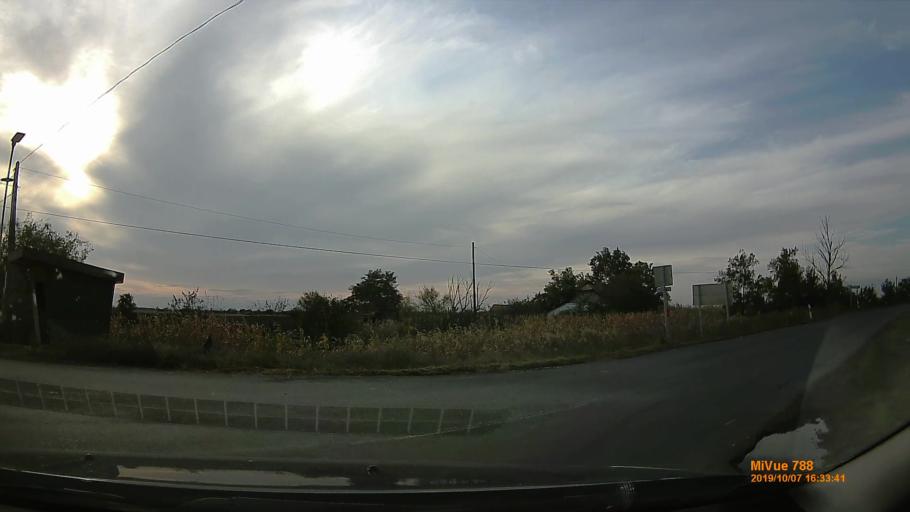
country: HU
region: Bekes
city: Szarvas
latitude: 46.7932
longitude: 20.6244
